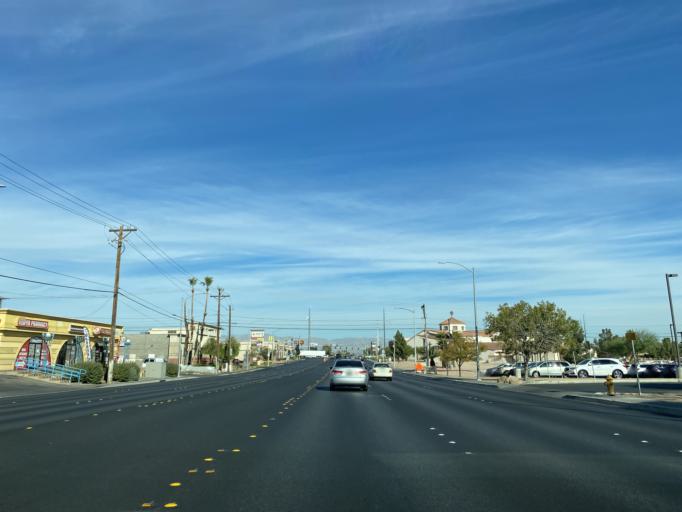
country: US
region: Nevada
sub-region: Clark County
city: Winchester
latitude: 36.1121
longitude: -115.1192
